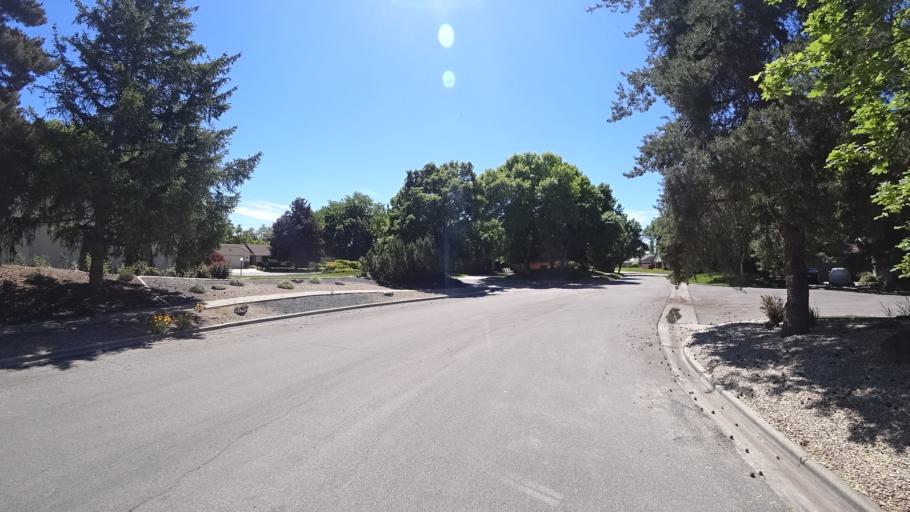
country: US
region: Idaho
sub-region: Ada County
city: Boise
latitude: 43.5858
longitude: -116.1725
